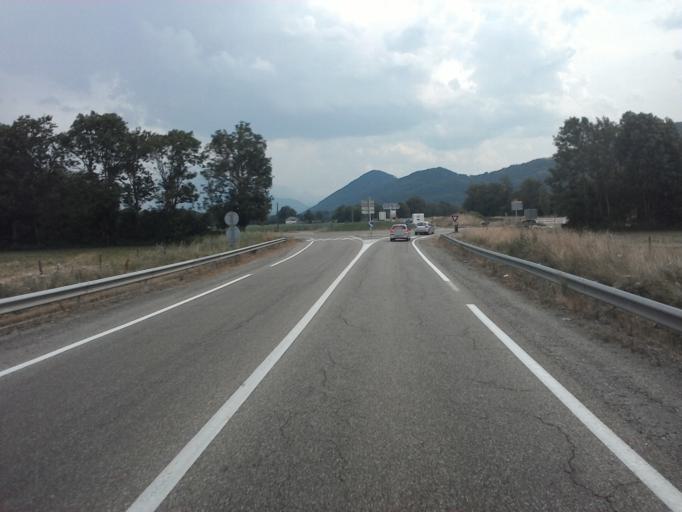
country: FR
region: Rhone-Alpes
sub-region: Departement de l'Isere
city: Pierre-Chatel
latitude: 44.9496
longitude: 5.7800
